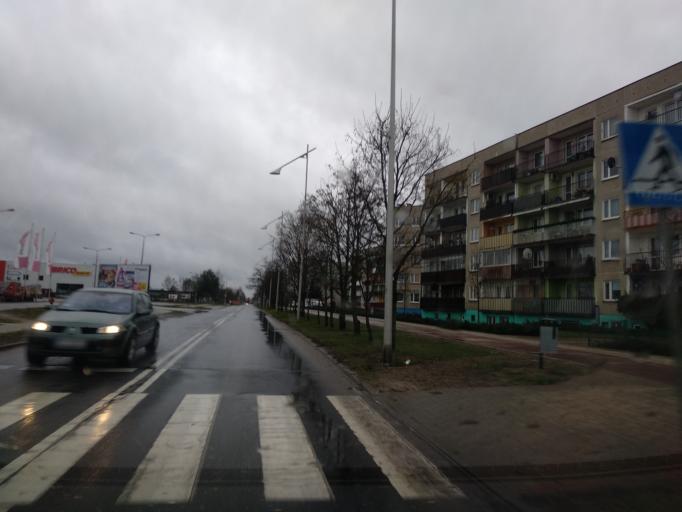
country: PL
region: Lower Silesian Voivodeship
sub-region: Powiat polkowicki
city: Polkowice
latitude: 51.5105
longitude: 16.0803
